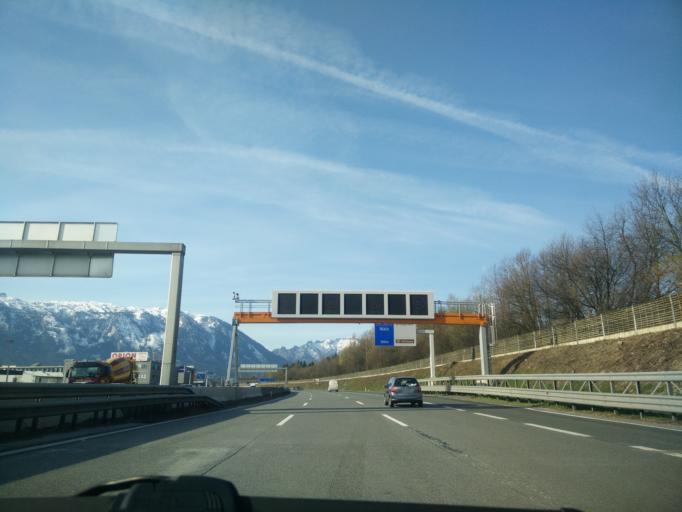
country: DE
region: Bavaria
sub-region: Upper Bavaria
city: Ainring
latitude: 47.7948
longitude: 12.9846
